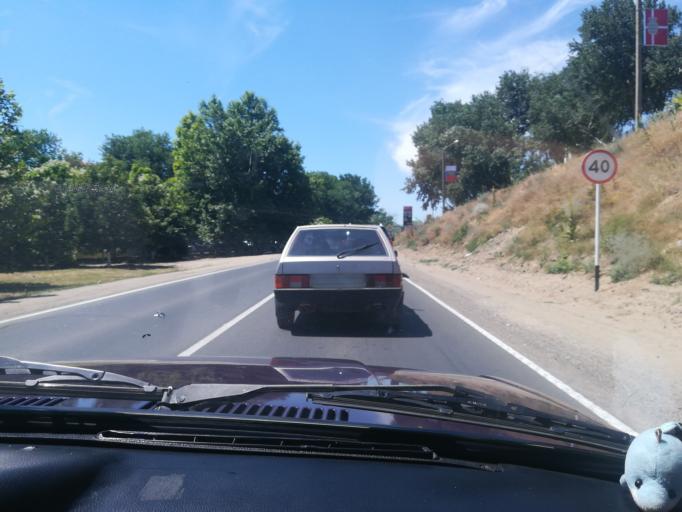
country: RU
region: Krasnodarskiy
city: Vityazevo
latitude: 44.9758
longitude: 37.2747
